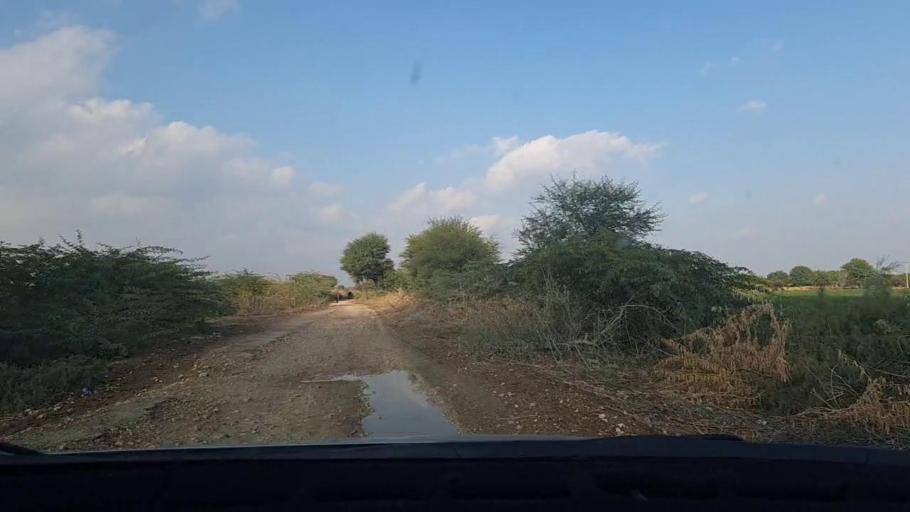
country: PK
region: Sindh
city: Tando Mittha Khan
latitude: 25.8821
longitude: 69.2878
